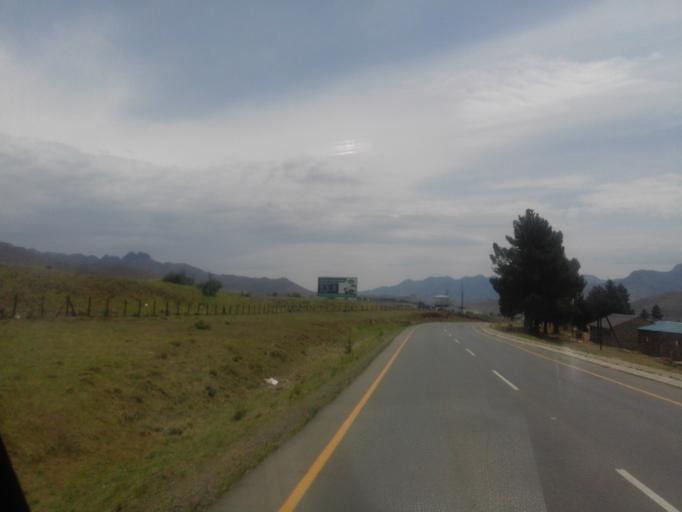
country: LS
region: Qacha's Nek
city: Qacha's Nek
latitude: -30.1112
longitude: 28.6739
